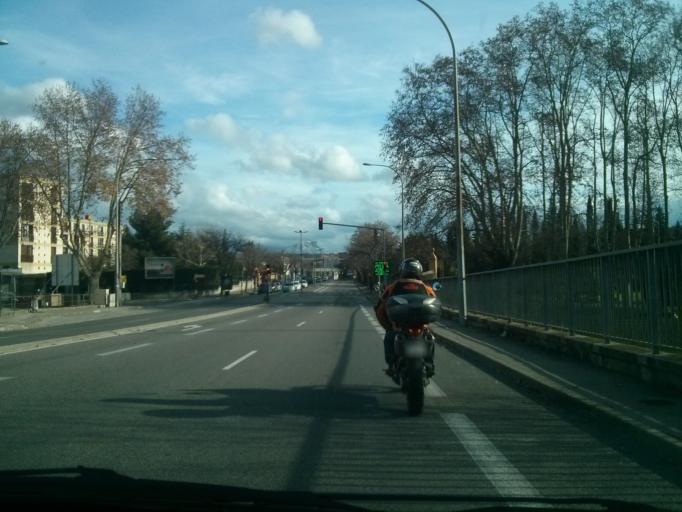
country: FR
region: Provence-Alpes-Cote d'Azur
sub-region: Departement des Bouches-du-Rhone
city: Aix-en-Provence
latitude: 43.5283
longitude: 5.4284
